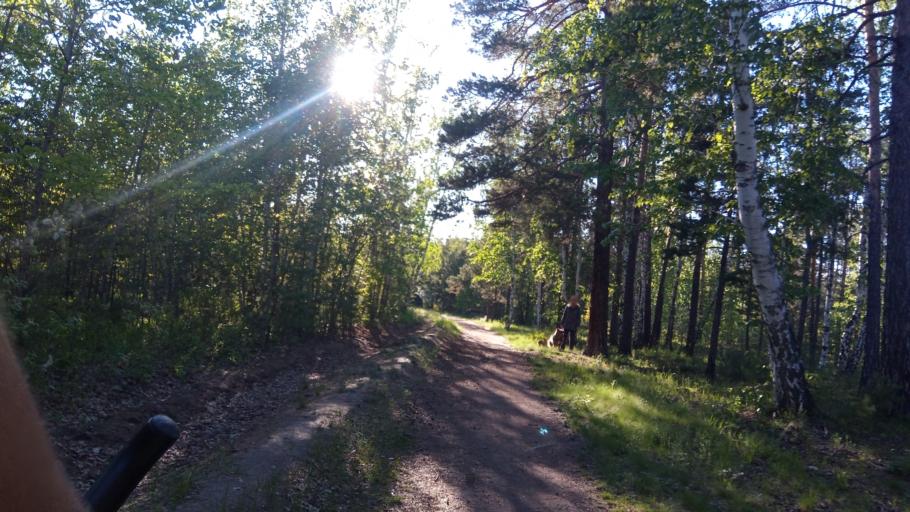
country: RU
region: Chelyabinsk
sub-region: Gorod Chelyabinsk
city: Chelyabinsk
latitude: 55.1264
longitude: 61.3433
